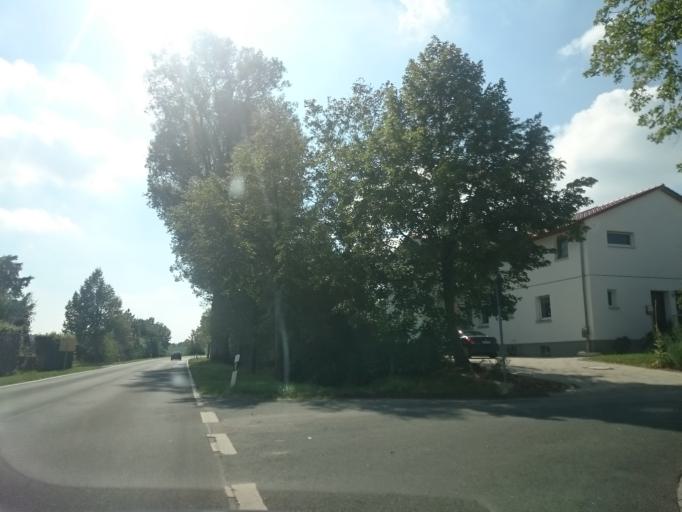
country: DE
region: Bavaria
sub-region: Regierungsbezirk Mittelfranken
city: Thalmassing
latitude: 49.1419
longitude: 11.2627
